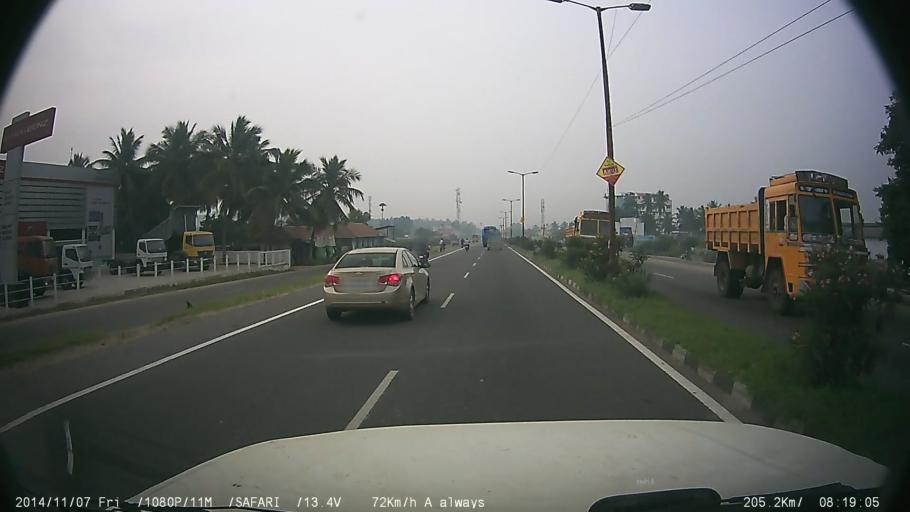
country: IN
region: Tamil Nadu
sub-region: Salem
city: Salem
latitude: 11.6532
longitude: 78.1211
